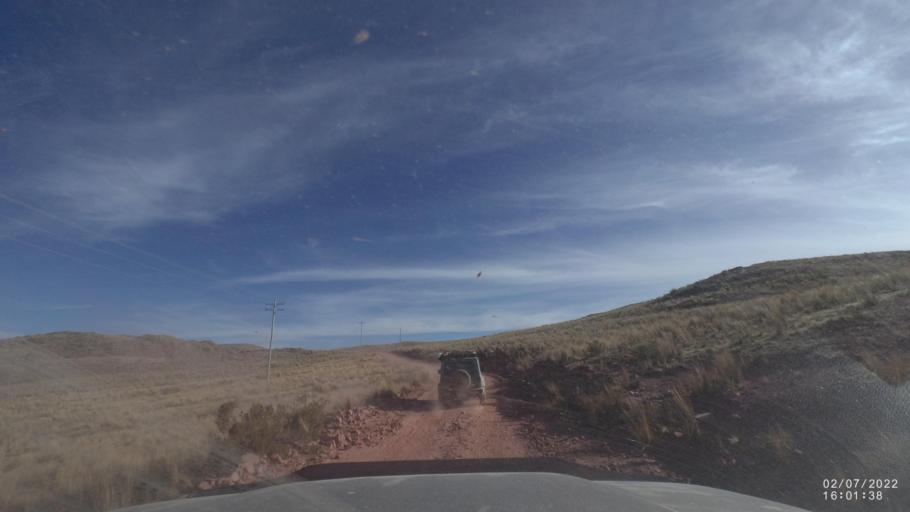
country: BO
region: Cochabamba
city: Irpa Irpa
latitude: -17.9074
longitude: -66.4390
